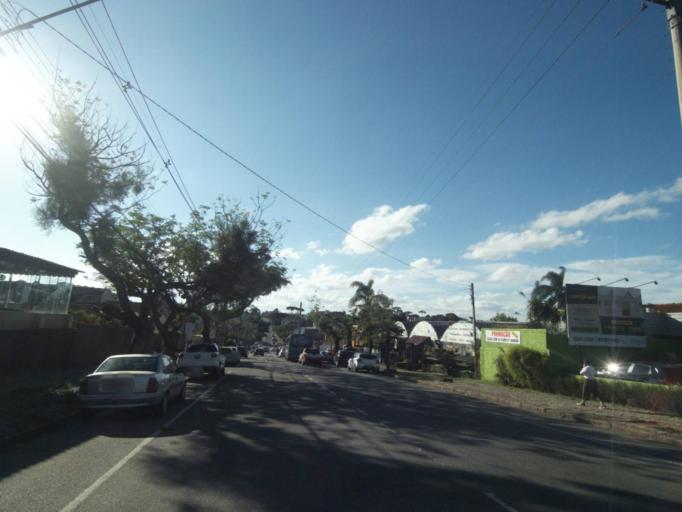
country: BR
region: Parana
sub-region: Curitiba
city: Curitiba
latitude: -25.3964
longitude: -49.2498
